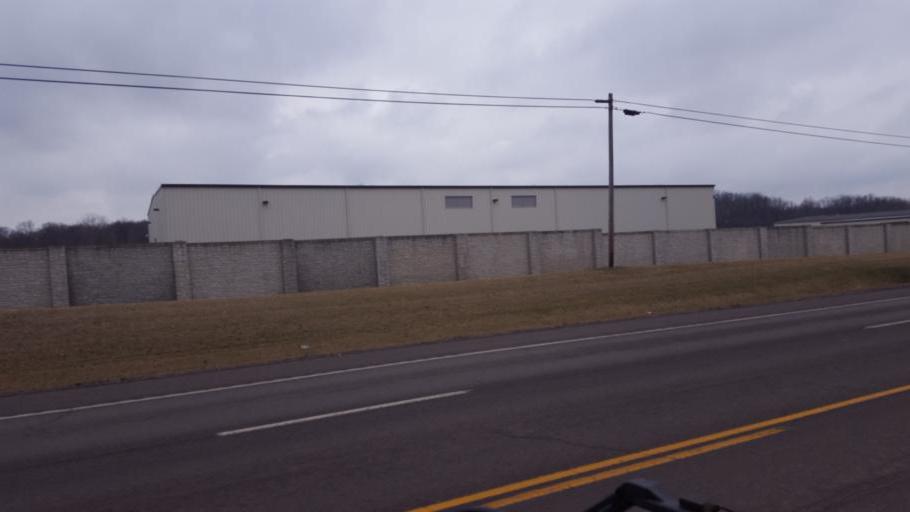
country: US
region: Ohio
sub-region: Richland County
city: Ontario
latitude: 40.8172
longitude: -82.5918
